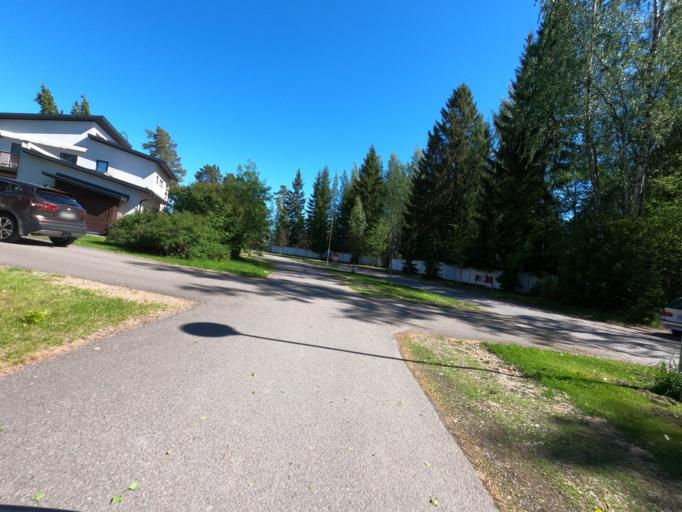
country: FI
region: North Karelia
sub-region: Joensuu
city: Joensuu
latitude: 62.5759
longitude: 29.7689
